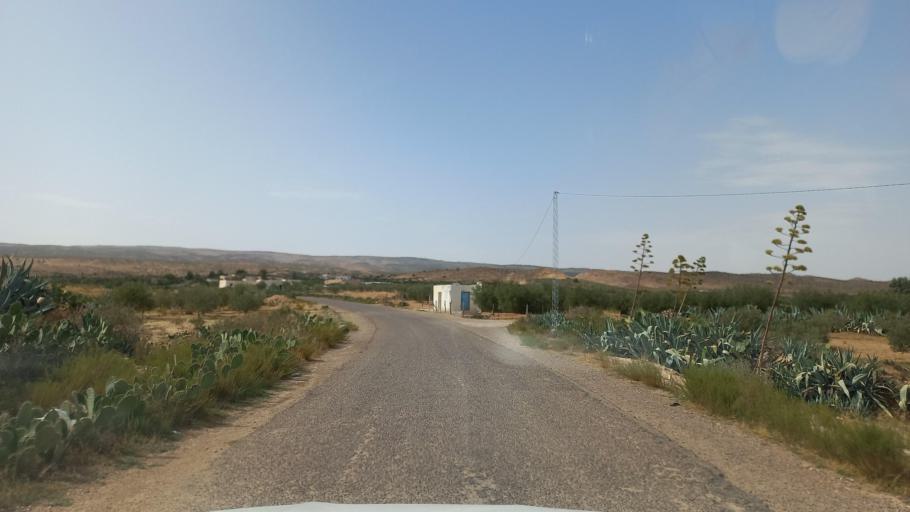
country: TN
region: Al Qasrayn
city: Kasserine
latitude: 35.2985
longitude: 8.9557
